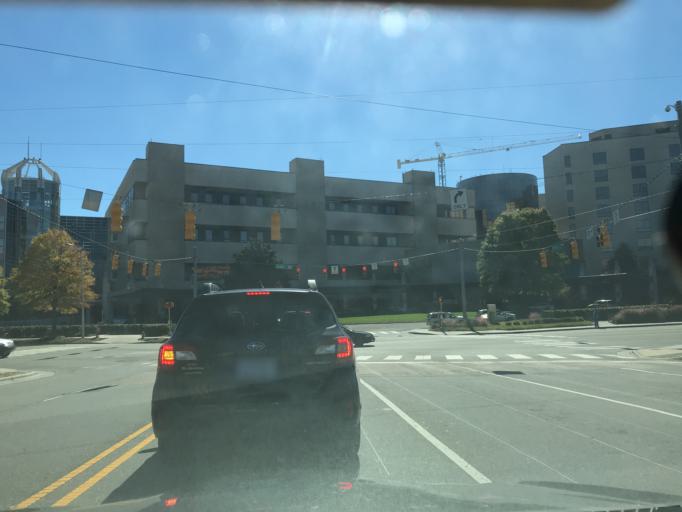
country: US
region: North Carolina
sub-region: Durham County
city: Durham
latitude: 36.0086
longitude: -78.9373
